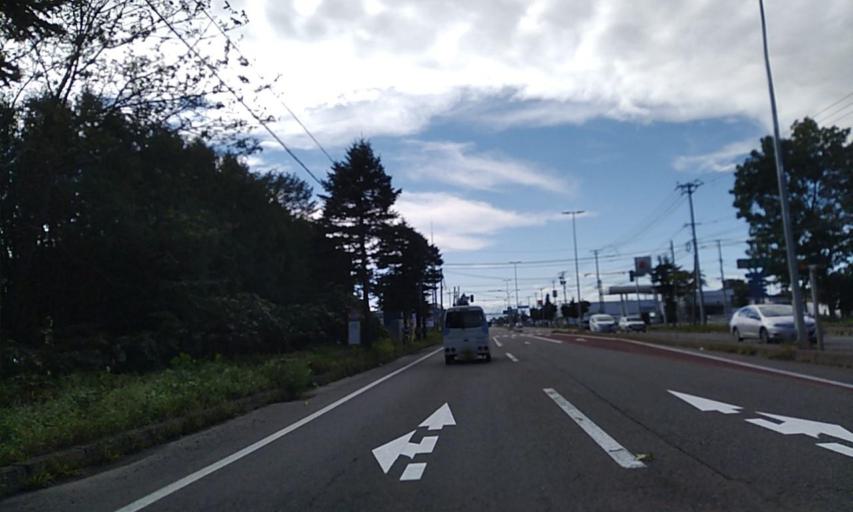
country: JP
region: Hokkaido
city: Obihiro
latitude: 42.9164
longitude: 143.2687
